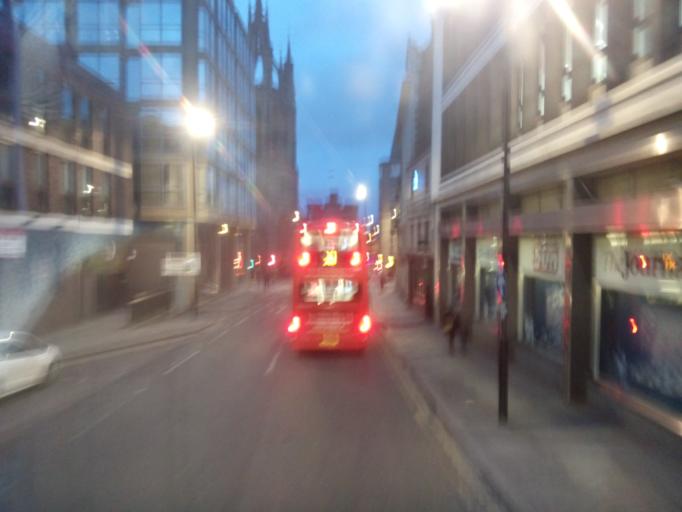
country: GB
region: England
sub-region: Newcastle upon Tyne
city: Newcastle upon Tyne
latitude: 54.9711
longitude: -1.6126
